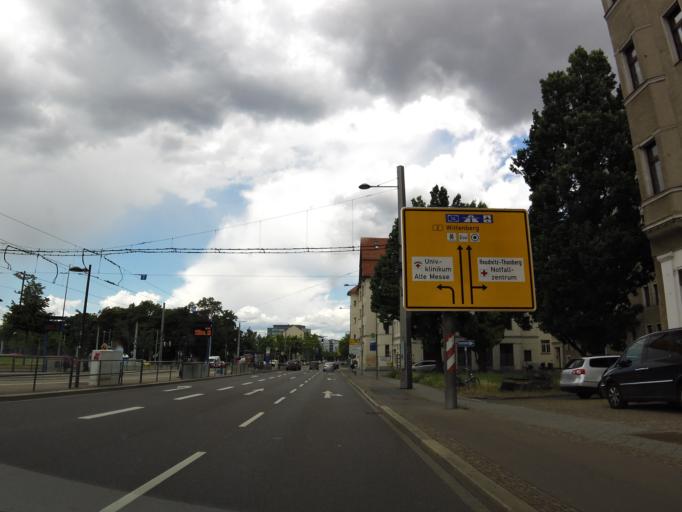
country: DE
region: Saxony
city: Leipzig
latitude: 51.3208
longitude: 12.4048
